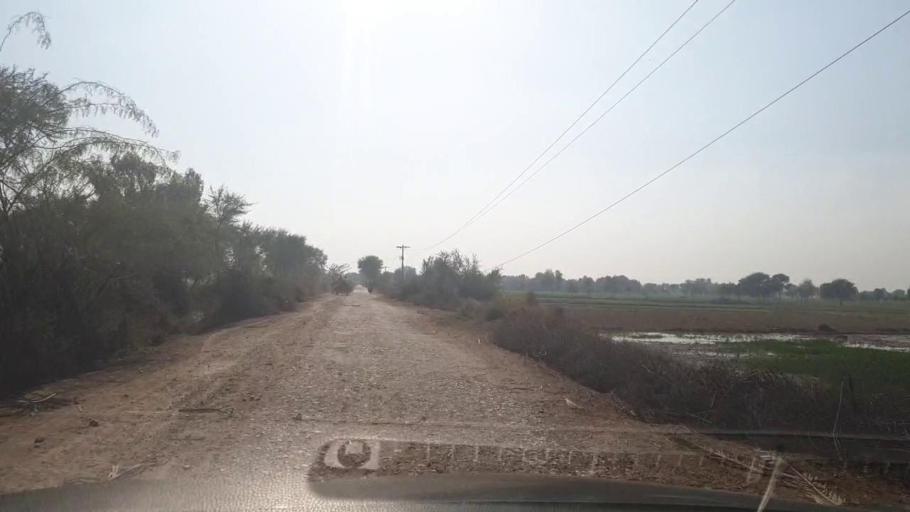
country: PK
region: Sindh
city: Ubauro
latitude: 28.1413
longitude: 69.6501
